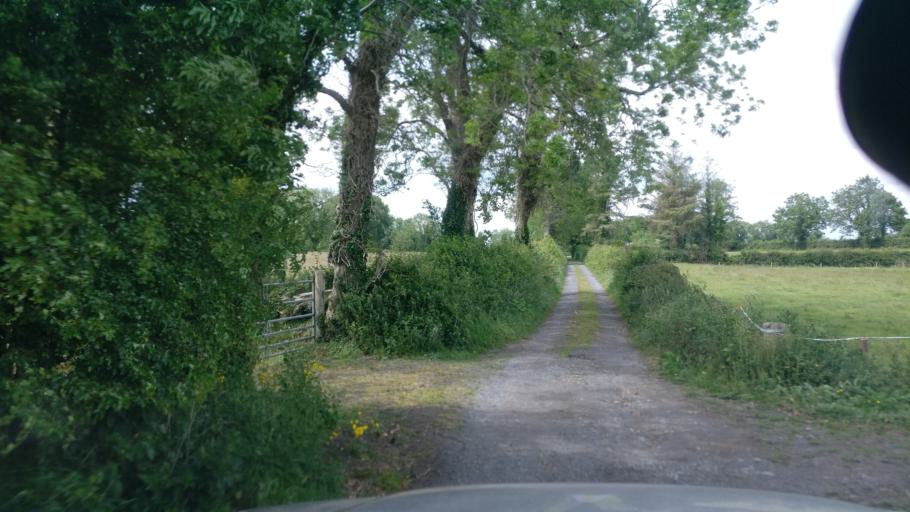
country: IE
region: Connaught
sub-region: County Galway
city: Ballinasloe
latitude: 53.2683
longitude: -8.3315
